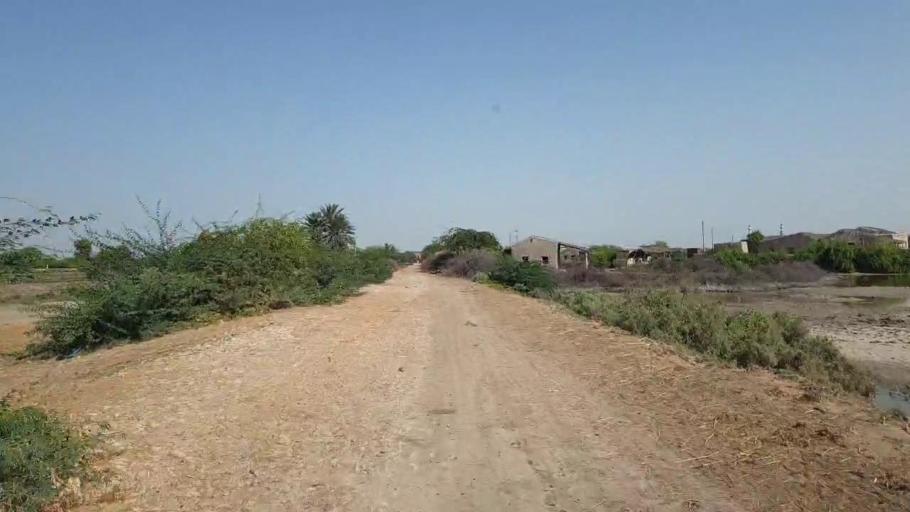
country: PK
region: Sindh
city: Tando Bago
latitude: 24.7242
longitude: 69.0261
